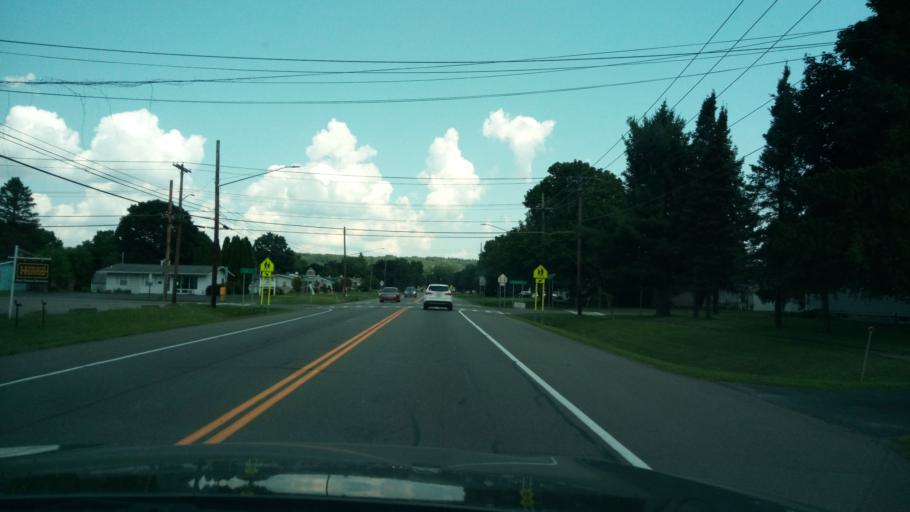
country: US
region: New York
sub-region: Chemung County
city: Horseheads
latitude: 42.1690
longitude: -76.8402
